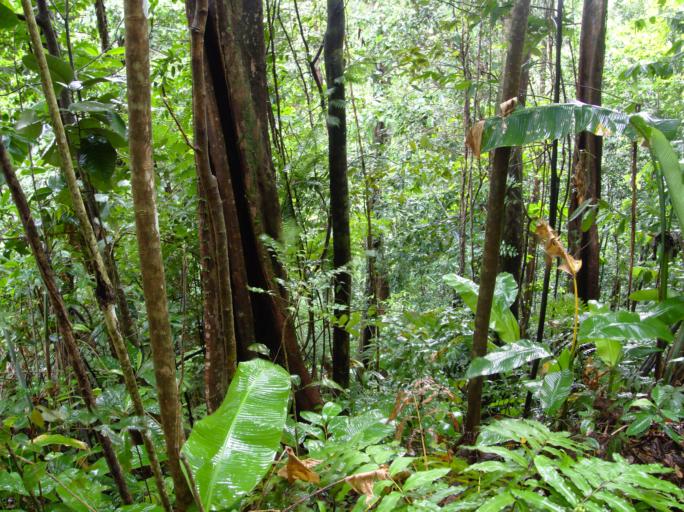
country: MQ
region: Martinique
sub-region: Martinique
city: Saint-Joseph
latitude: 14.6774
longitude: -61.0973
